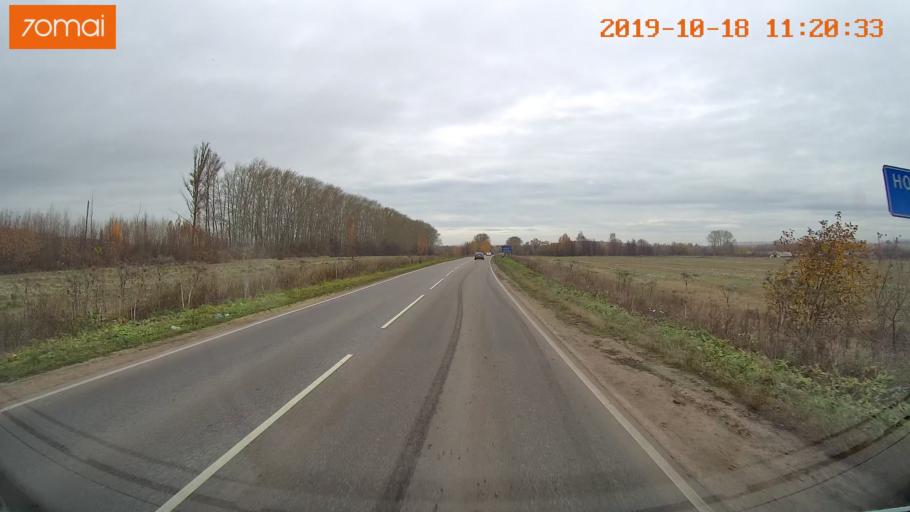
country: RU
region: Tula
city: Kimovsk
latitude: 54.0624
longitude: 38.5591
